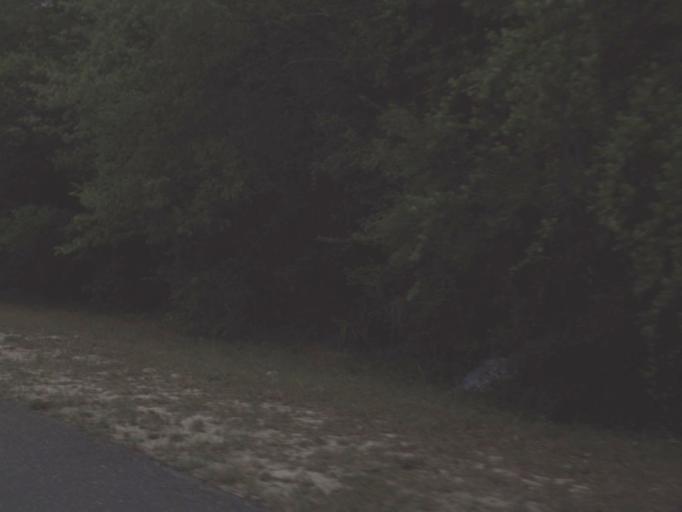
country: US
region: Florida
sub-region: Marion County
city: Ocala
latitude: 29.2320
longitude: -82.0430
